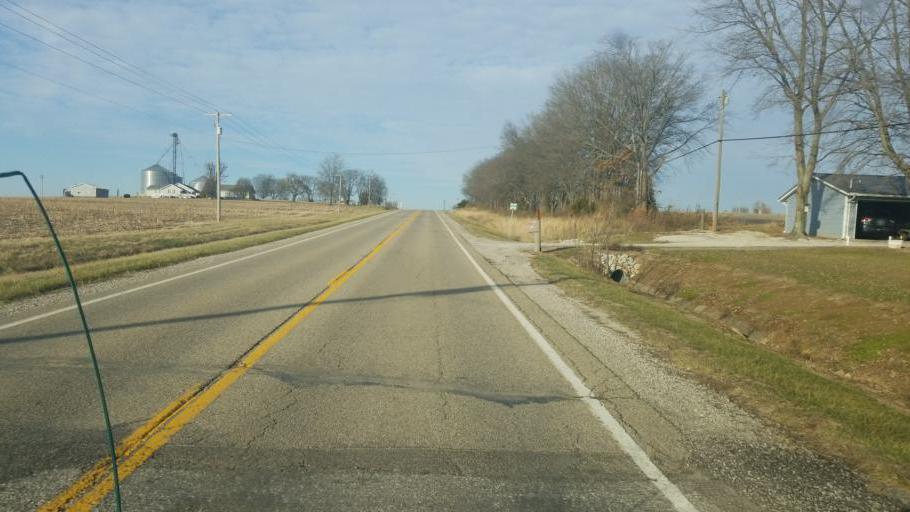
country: US
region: Illinois
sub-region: Lawrence County
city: Lawrenceville
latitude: 38.6552
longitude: -87.6942
